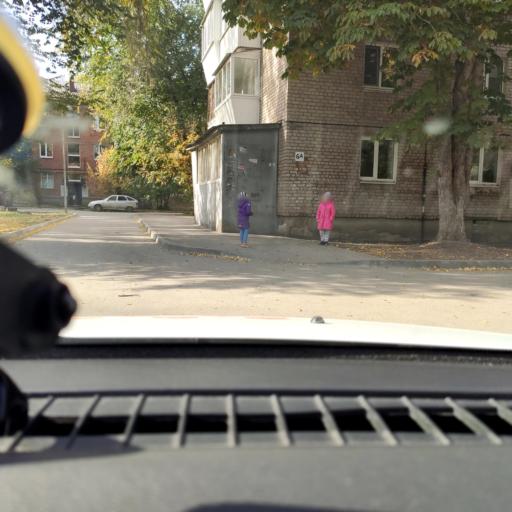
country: RU
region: Samara
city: Smyshlyayevka
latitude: 53.2304
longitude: 50.2976
